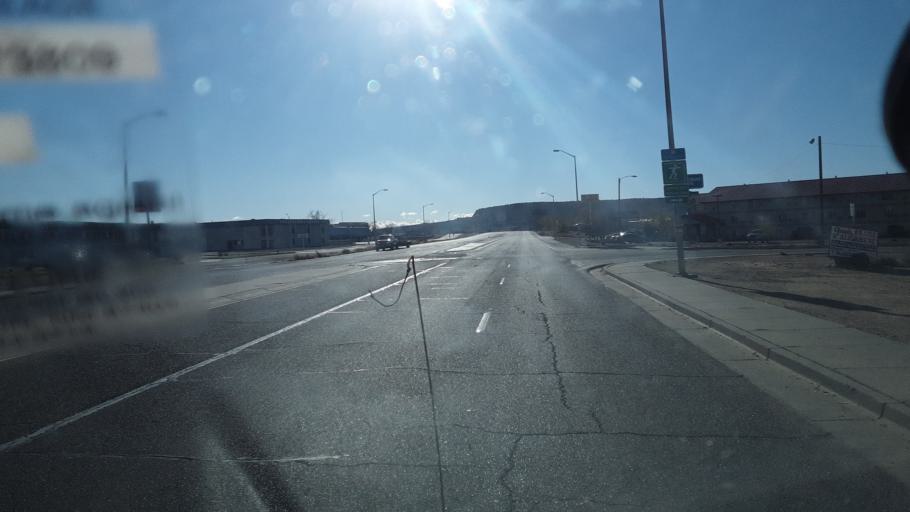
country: US
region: New Mexico
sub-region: San Juan County
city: Farmington
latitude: 36.7250
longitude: -108.1893
